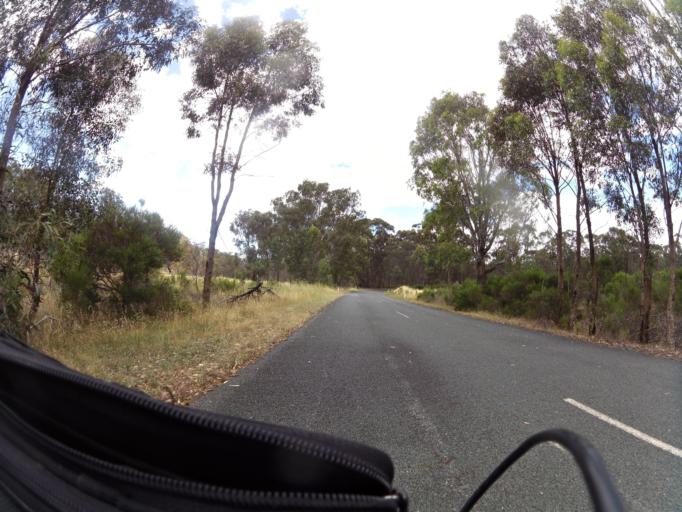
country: AU
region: Victoria
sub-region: Greater Shepparton
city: Shepparton
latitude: -36.6866
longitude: 145.1805
